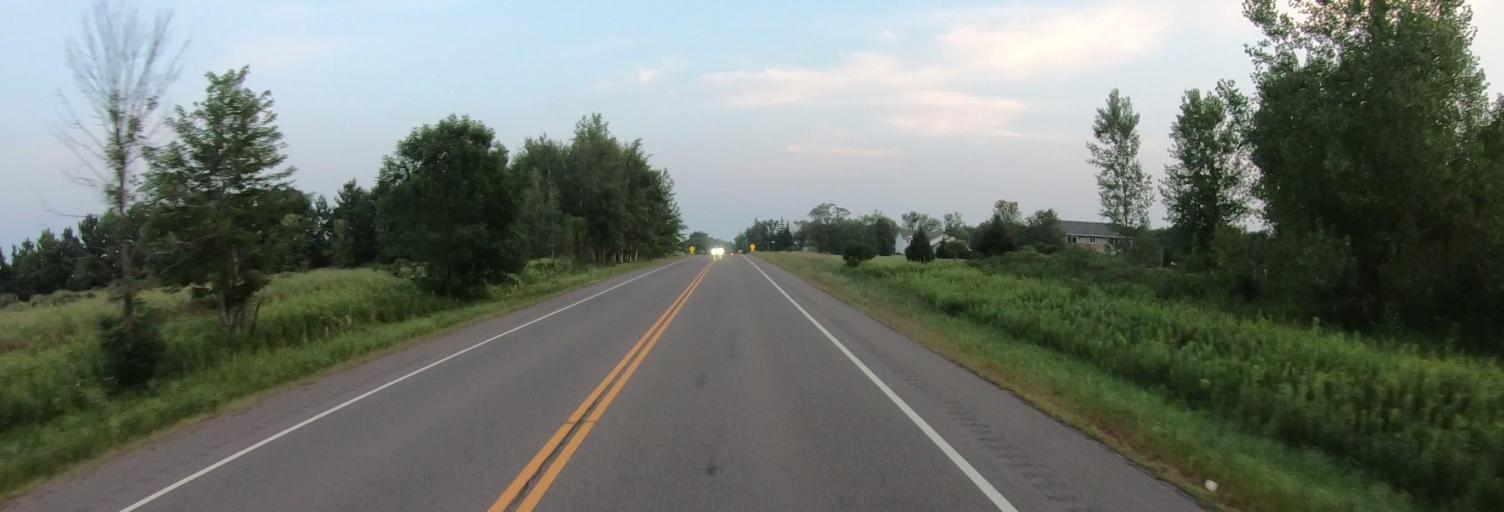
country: US
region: Minnesota
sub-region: Pine County
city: Rock Creek
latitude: 45.7698
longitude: -92.9602
